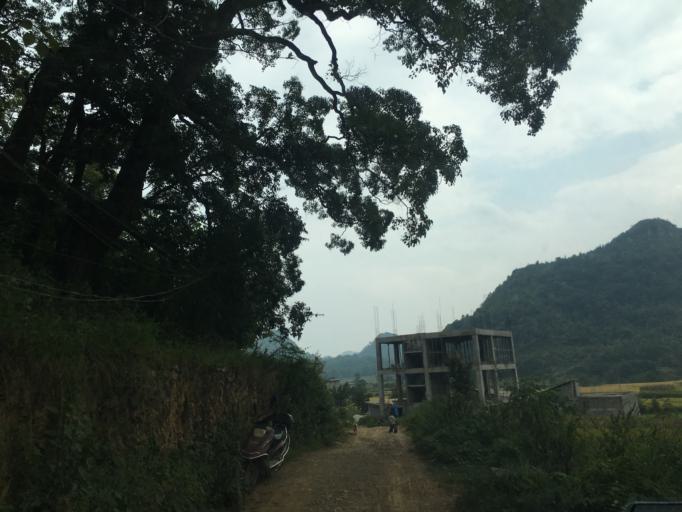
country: CN
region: Guangxi Zhuangzu Zizhiqu
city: Xinzhou
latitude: 25.4980
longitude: 105.6490
